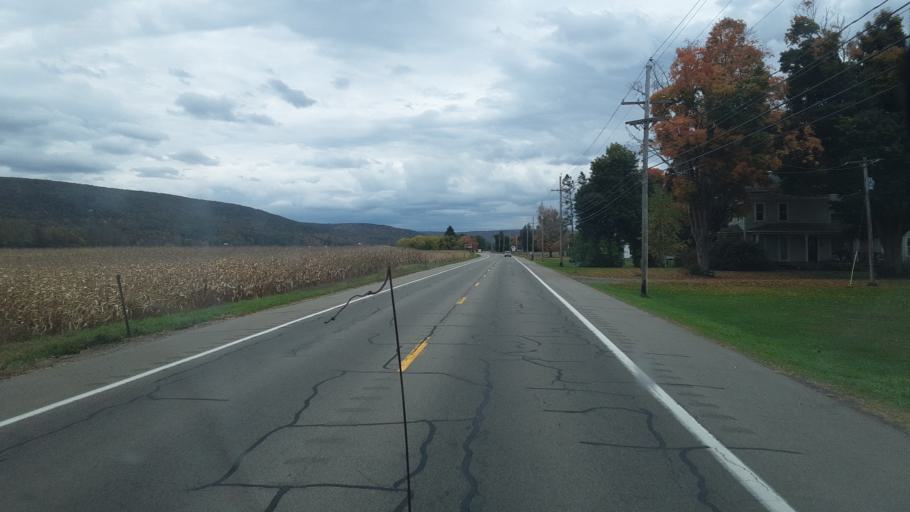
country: US
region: New York
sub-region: Allegany County
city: Belmont
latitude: 42.2075
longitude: -78.0123
